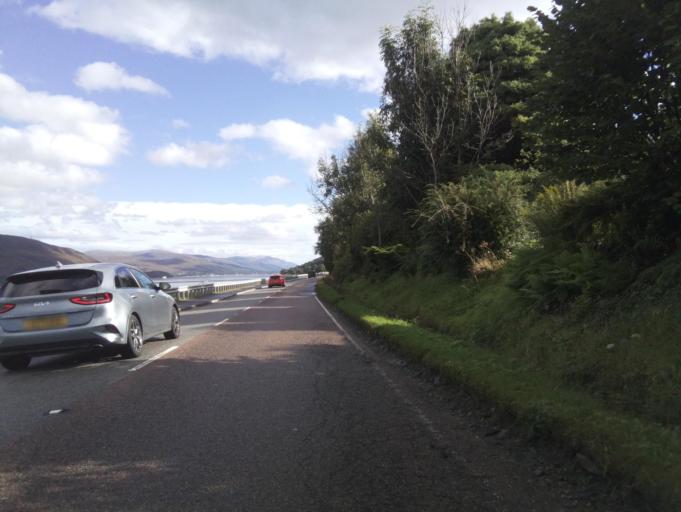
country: GB
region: Scotland
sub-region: Highland
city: Fort William
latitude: 56.7899
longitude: -5.1504
